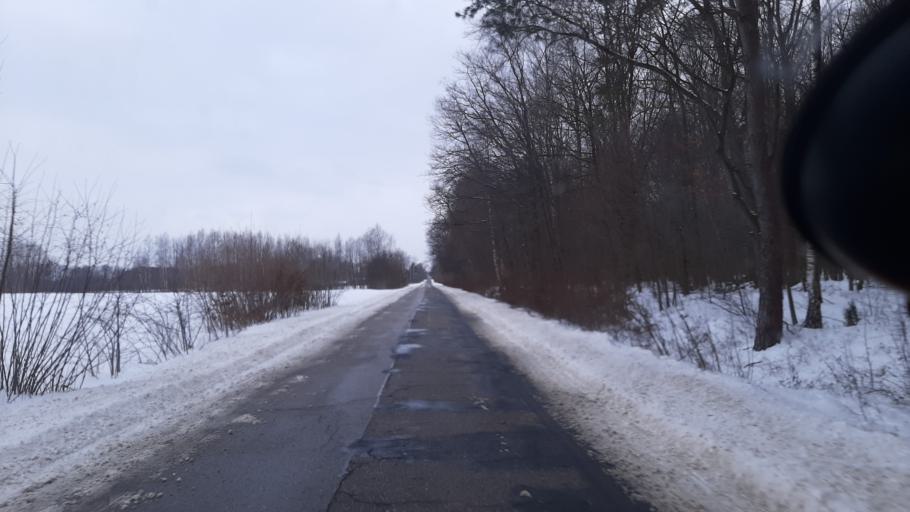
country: PL
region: Lublin Voivodeship
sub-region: Powiat pulawski
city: Markuszow
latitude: 51.4360
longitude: 22.2432
